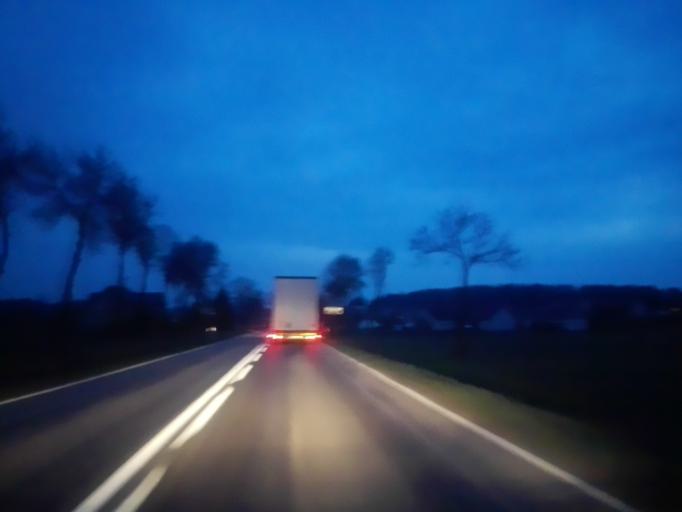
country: PL
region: Podlasie
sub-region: Powiat lomzynski
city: Sniadowo
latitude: 53.0636
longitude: 22.0045
